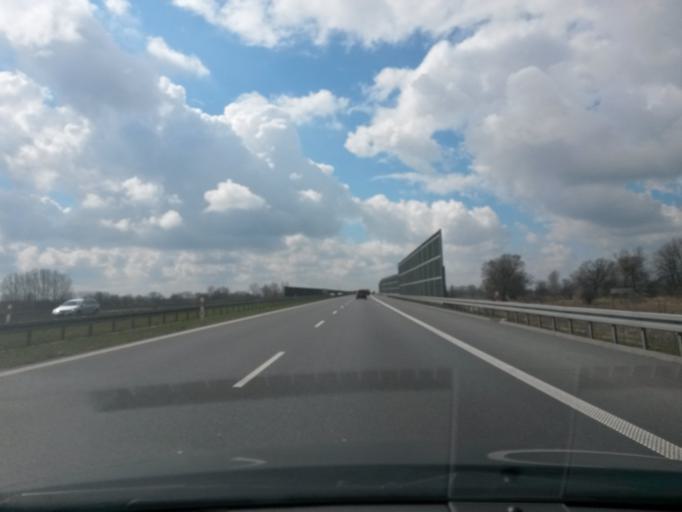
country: PL
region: Masovian Voivodeship
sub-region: Powiat warszawski zachodni
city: Bieniewice
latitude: 52.1206
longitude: 20.5127
